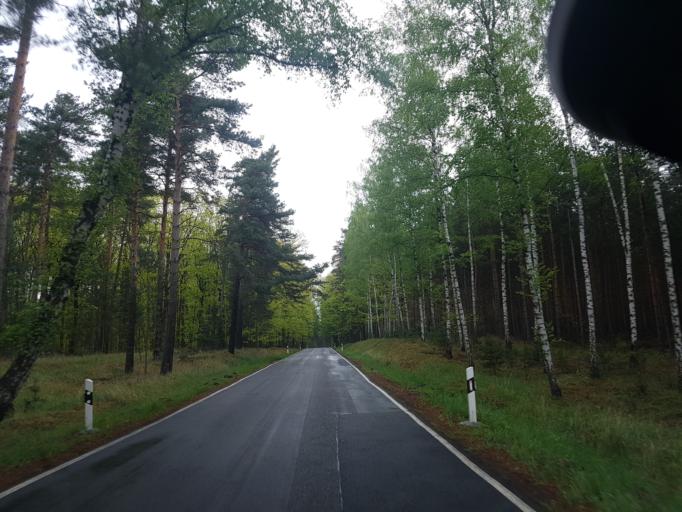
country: DE
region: Brandenburg
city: Spremberg
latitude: 51.6248
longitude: 14.4212
